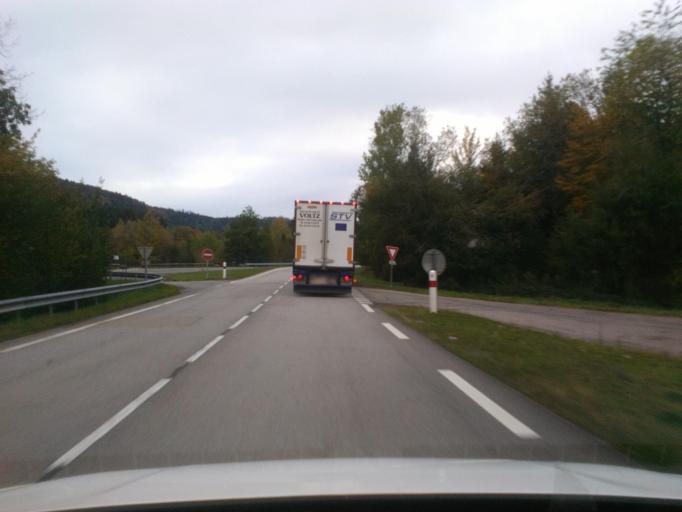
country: FR
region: Lorraine
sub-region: Departement des Vosges
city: Ban-de-Laveline
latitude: 48.3332
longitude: 7.0972
